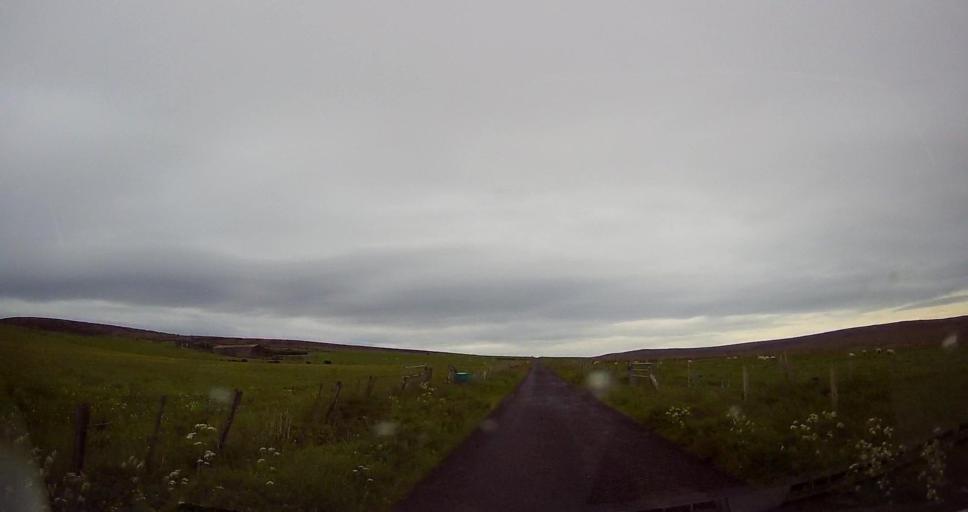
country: GB
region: Scotland
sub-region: Orkney Islands
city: Stromness
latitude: 59.0937
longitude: -3.1777
